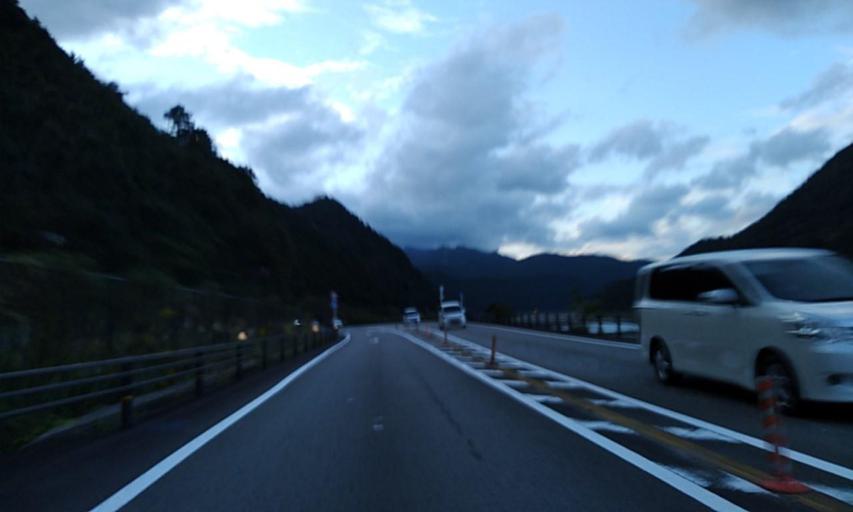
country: JP
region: Wakayama
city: Shingu
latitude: 33.7262
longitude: 135.9548
